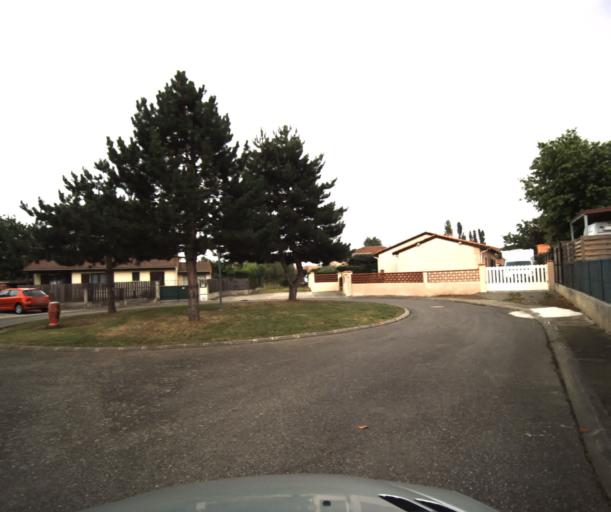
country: FR
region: Midi-Pyrenees
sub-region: Departement de la Haute-Garonne
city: Pinsaguel
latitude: 43.4980
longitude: 1.3939
